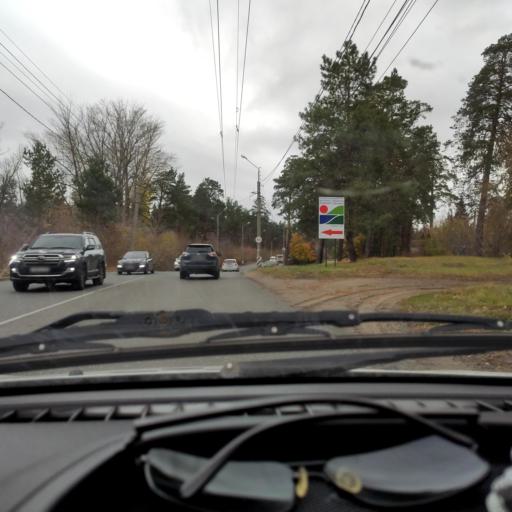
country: RU
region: Samara
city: Tol'yatti
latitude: 53.4779
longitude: 49.3624
